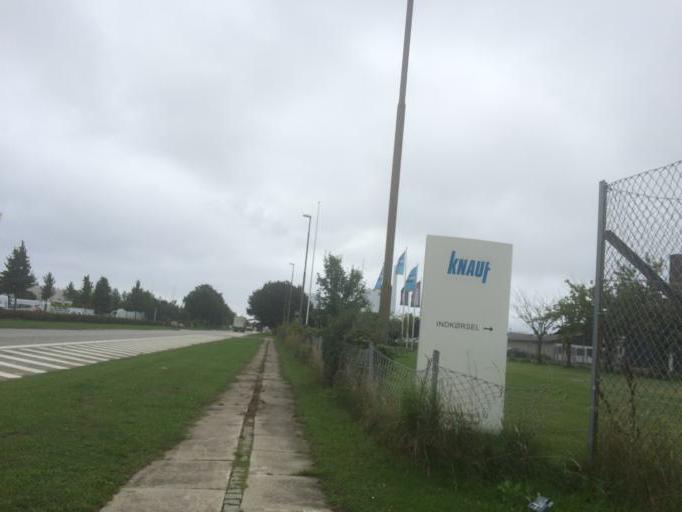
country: DK
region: Capital Region
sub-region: Hvidovre Kommune
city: Hvidovre
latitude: 55.6123
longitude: 12.4831
